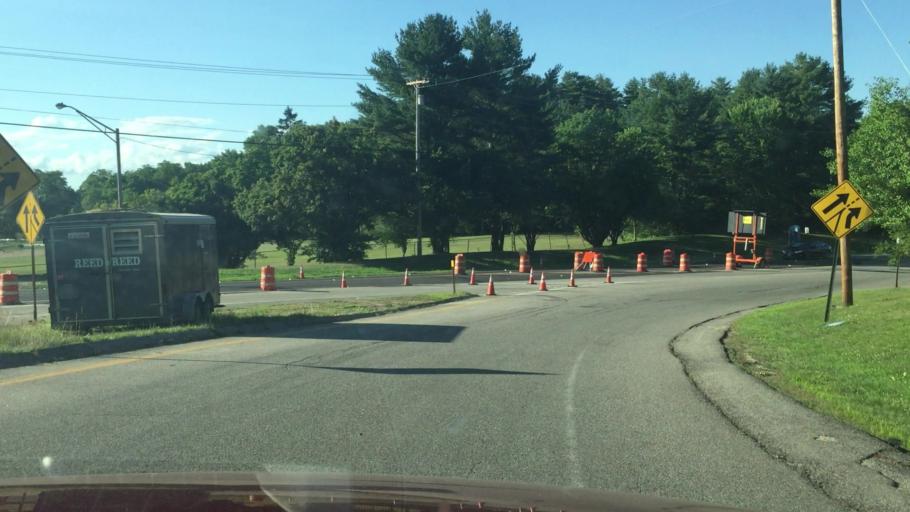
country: US
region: Maine
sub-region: Cumberland County
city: Yarmouth
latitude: 43.8013
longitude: -70.1857
